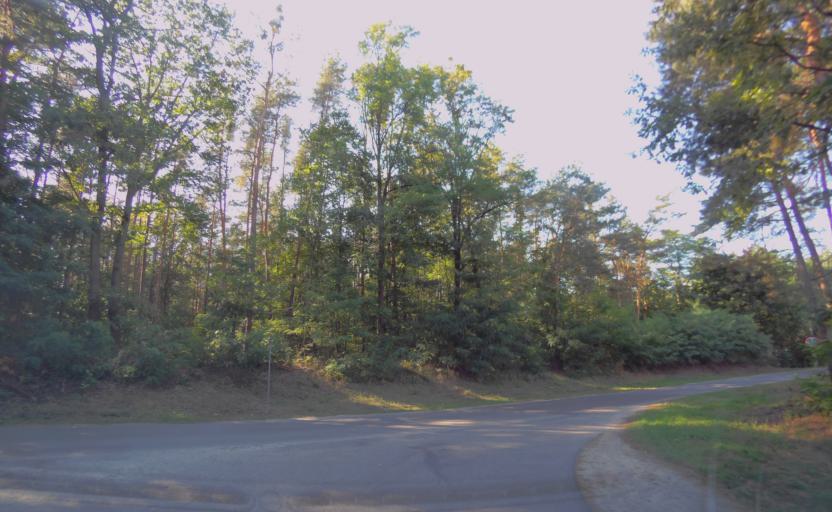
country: PL
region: Subcarpathian Voivodeship
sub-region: Powiat lezajski
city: Stare Miasto
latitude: 50.2913
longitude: 22.4021
